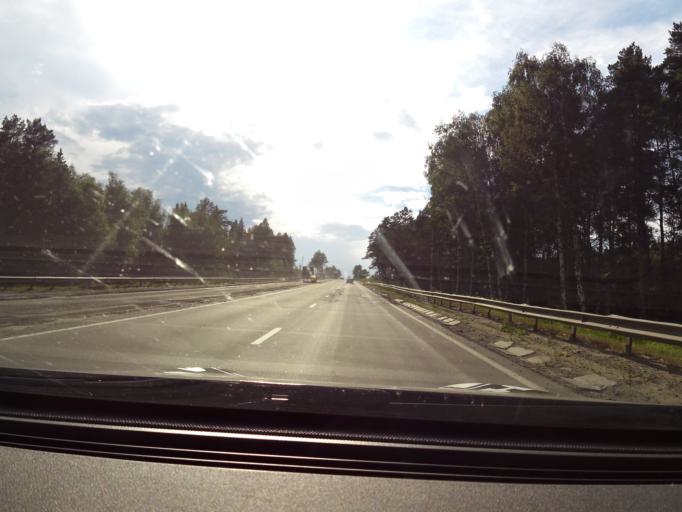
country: RU
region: Vladimir
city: Gorokhovets
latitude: 56.1681
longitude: 42.4563
